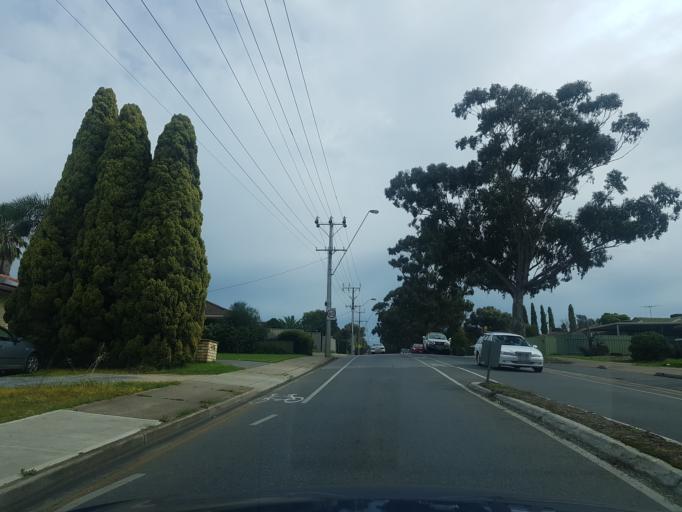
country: AU
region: South Australia
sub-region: Tea Tree Gully
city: Modbury
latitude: -34.8178
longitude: 138.6862
